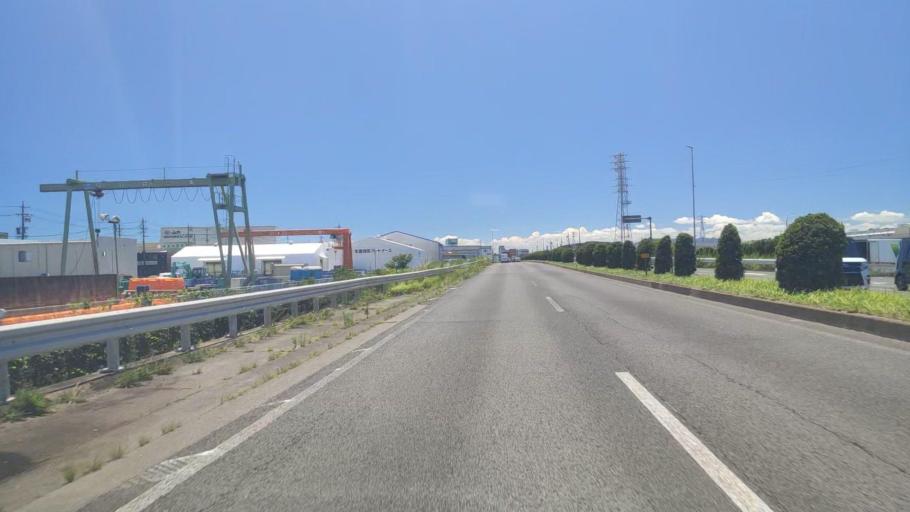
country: JP
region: Mie
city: Suzuka
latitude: 34.9195
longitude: 136.6111
